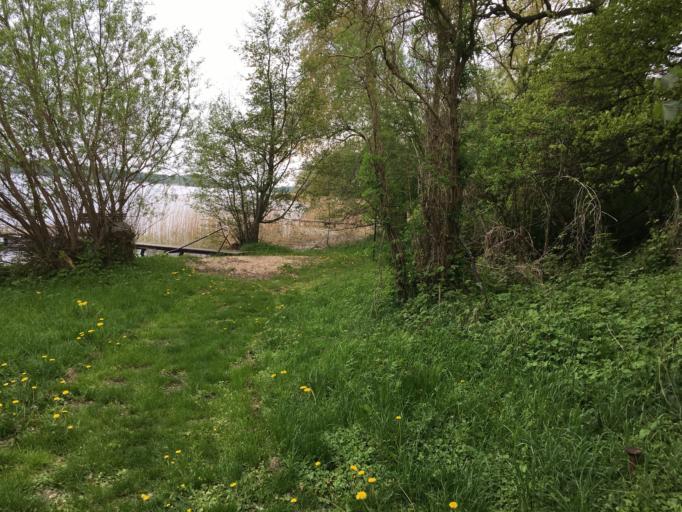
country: DE
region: Mecklenburg-Vorpommern
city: Krakow am See
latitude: 53.6623
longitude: 12.3129
